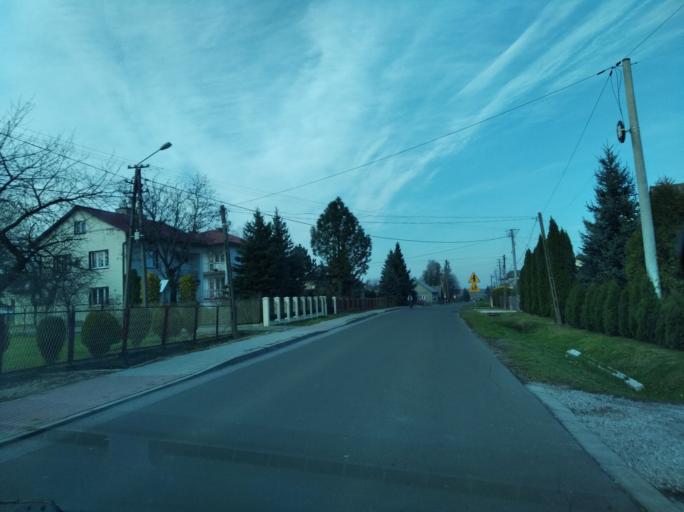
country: PL
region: Subcarpathian Voivodeship
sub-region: Powiat ropczycko-sedziszowski
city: Iwierzyce
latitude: 50.0113
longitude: 21.7538
